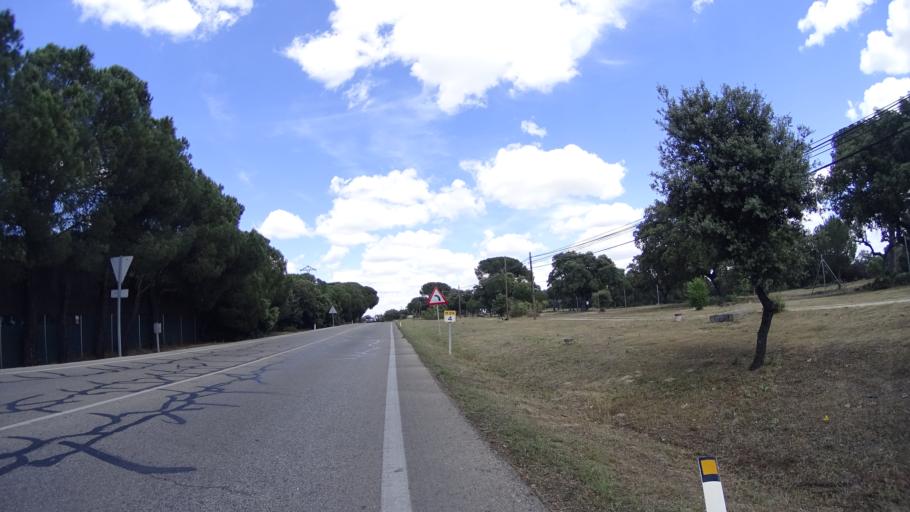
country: ES
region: Madrid
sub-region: Provincia de Madrid
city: Boadilla del Monte
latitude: 40.4185
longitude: -3.8773
